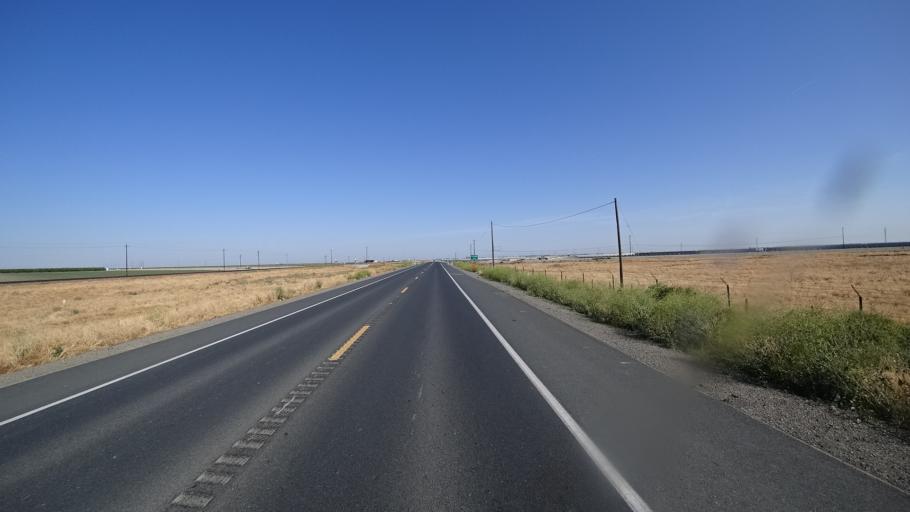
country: US
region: California
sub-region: Kings County
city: Corcoran
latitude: 36.1359
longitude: -119.5836
